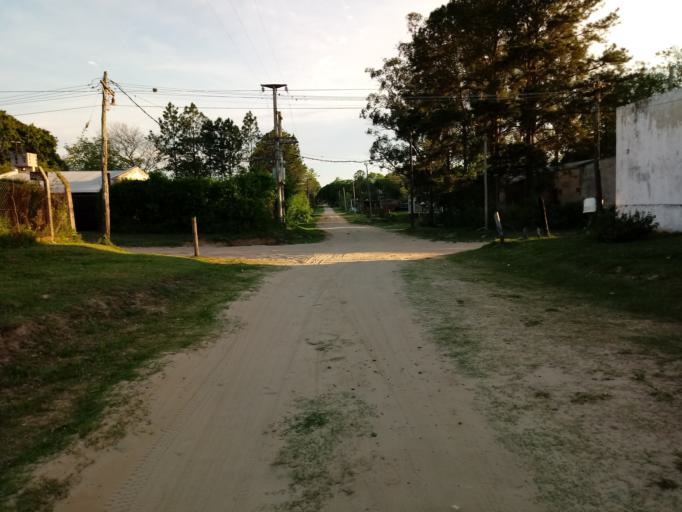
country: AR
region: Corrientes
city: San Luis del Palmar
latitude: -27.4529
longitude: -58.6575
